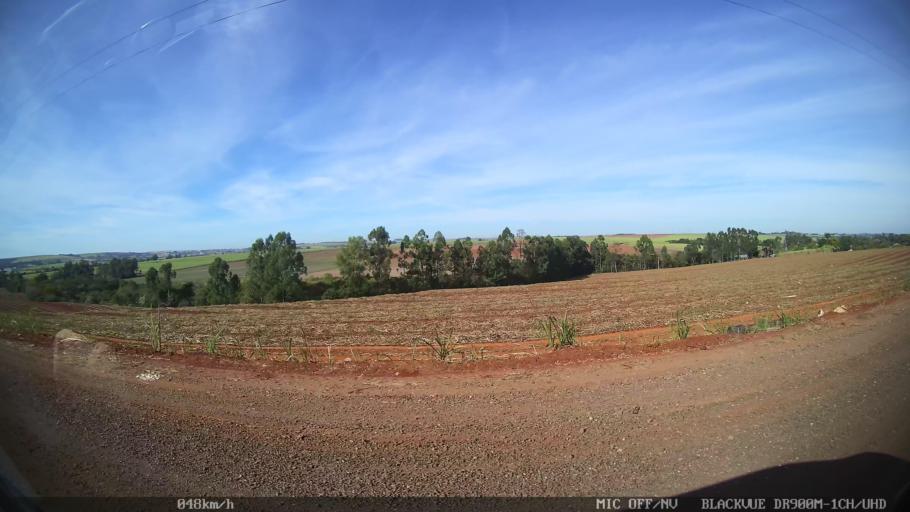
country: BR
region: Sao Paulo
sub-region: Rio Das Pedras
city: Rio das Pedras
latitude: -22.7898
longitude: -47.6425
